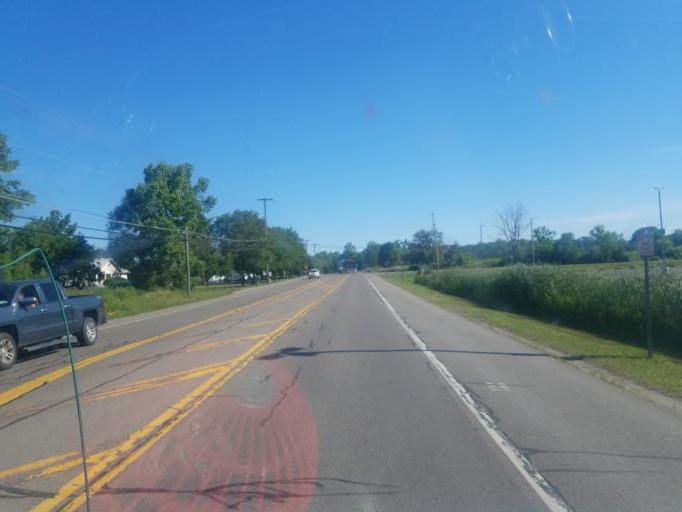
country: US
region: New York
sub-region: Ontario County
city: Canandaigua
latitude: 42.8648
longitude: -77.2507
